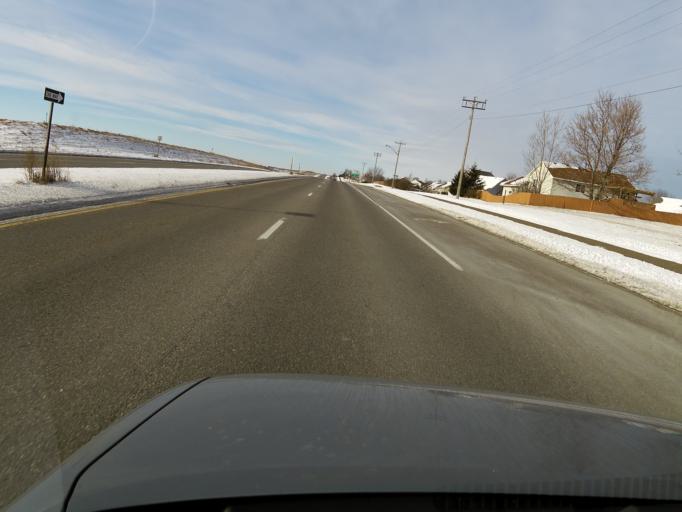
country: US
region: Minnesota
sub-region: Dakota County
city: Rosemount
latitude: 44.7174
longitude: -93.1416
